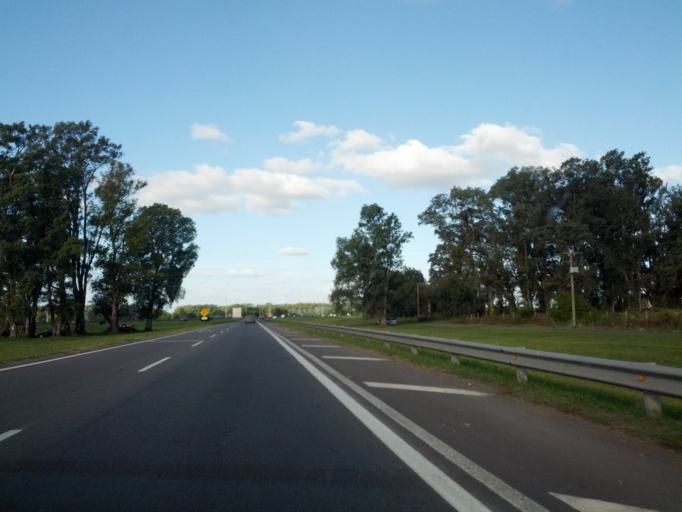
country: AR
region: Buenos Aires
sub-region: Partido de Lujan
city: Lujan
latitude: -34.5693
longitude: -59.0625
